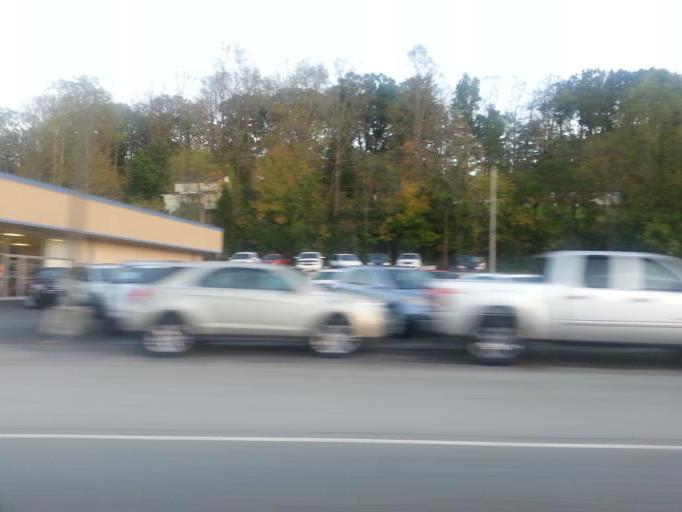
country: US
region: Tennessee
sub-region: Campbell County
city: Hunter
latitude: 36.3652
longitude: -84.1380
